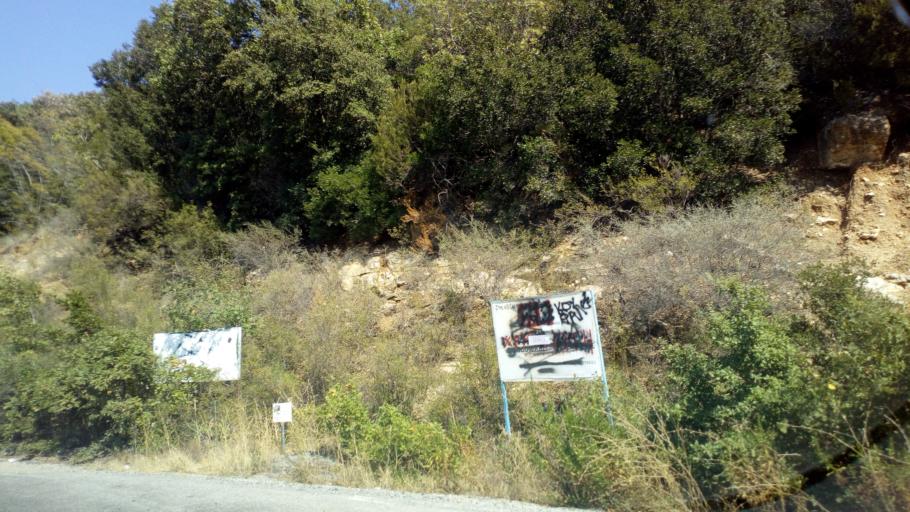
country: GR
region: Central Macedonia
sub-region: Nomos Thessalonikis
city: Stavros
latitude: 40.6552
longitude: 23.7329
